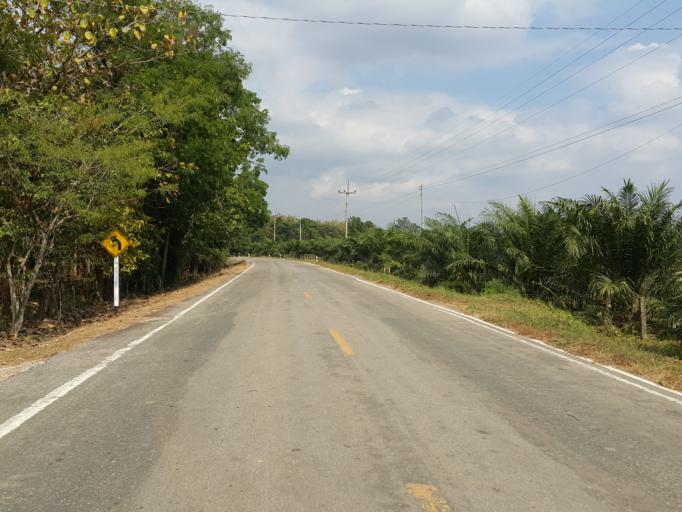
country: TH
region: Sukhothai
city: Thung Saliam
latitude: 17.3622
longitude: 99.5944
